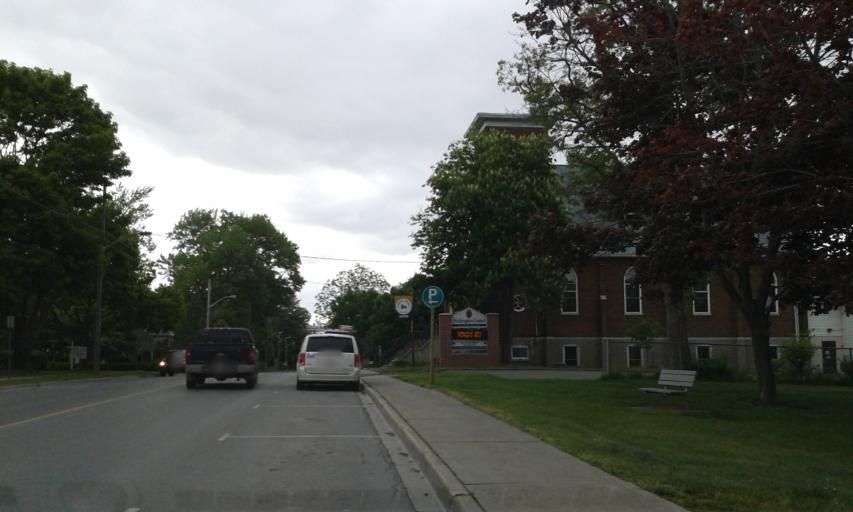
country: CA
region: Ontario
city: Prince Edward
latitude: 43.9518
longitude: -77.3479
